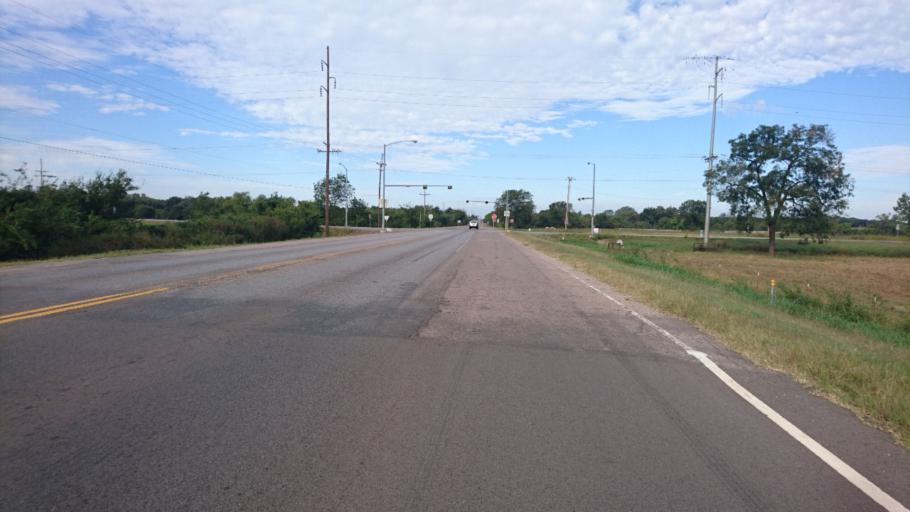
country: US
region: Oklahoma
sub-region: Lincoln County
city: Chandler
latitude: 35.6811
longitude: -97.0161
